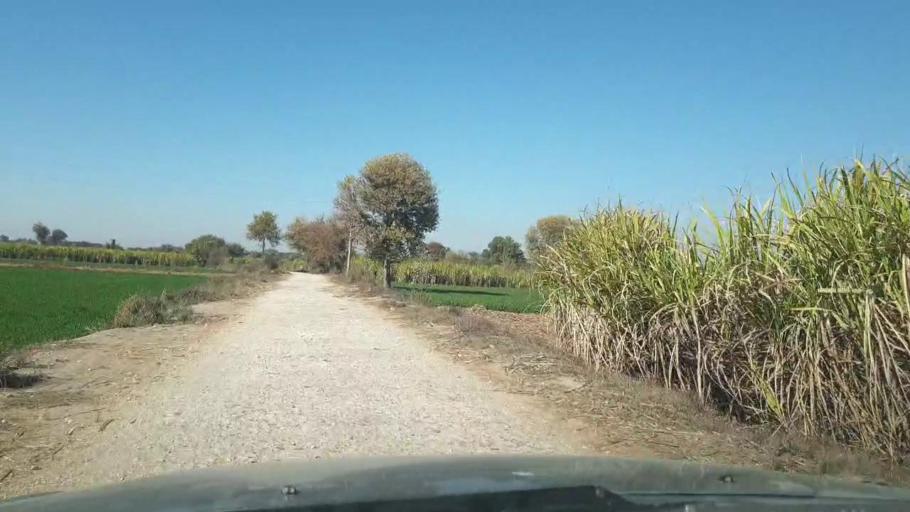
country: PK
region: Sindh
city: Ghotki
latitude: 28.0536
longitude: 69.2415
